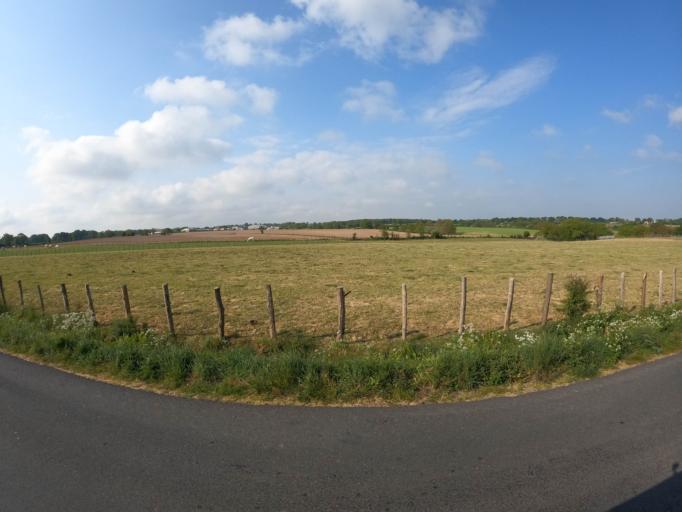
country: FR
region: Pays de la Loire
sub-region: Departement de Maine-et-Loire
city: Roussay
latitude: 47.0714
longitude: -1.0486
